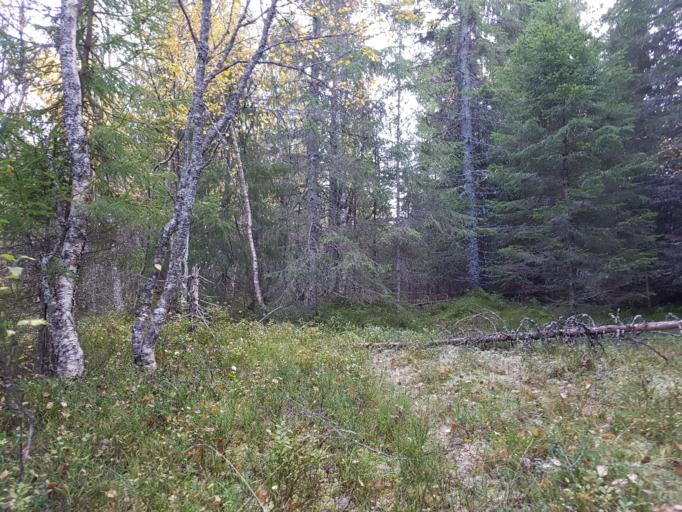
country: NO
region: Sor-Trondelag
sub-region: Trondheim
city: Trondheim
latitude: 63.4488
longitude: 10.2800
